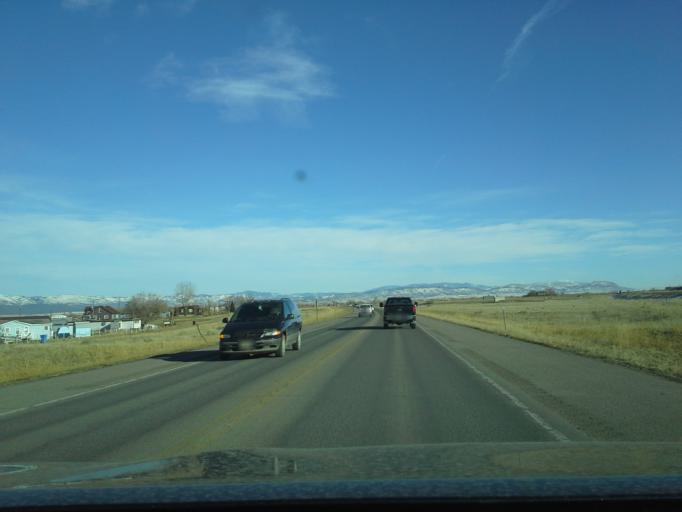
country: US
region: Montana
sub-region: Lewis and Clark County
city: Helena
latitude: 46.6165
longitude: -111.9868
